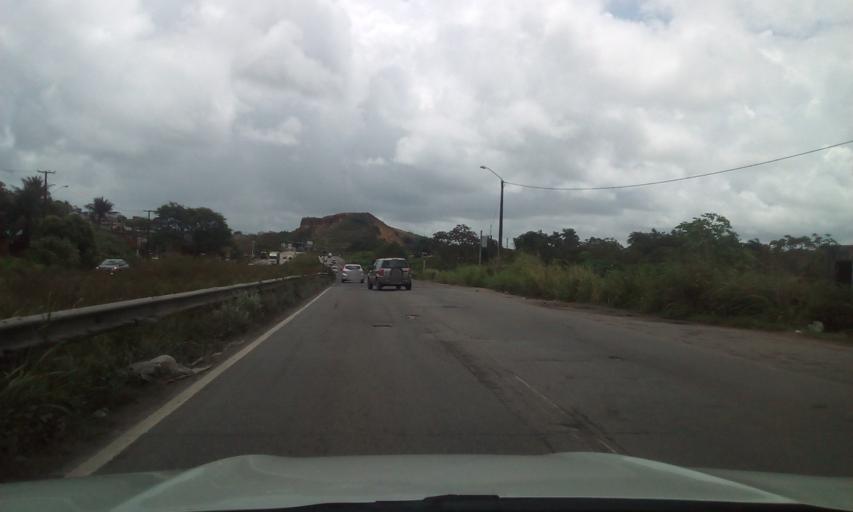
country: BR
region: Pernambuco
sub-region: Jaboatao Dos Guararapes
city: Jaboatao dos Guararapes
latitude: -8.1095
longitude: -34.9468
